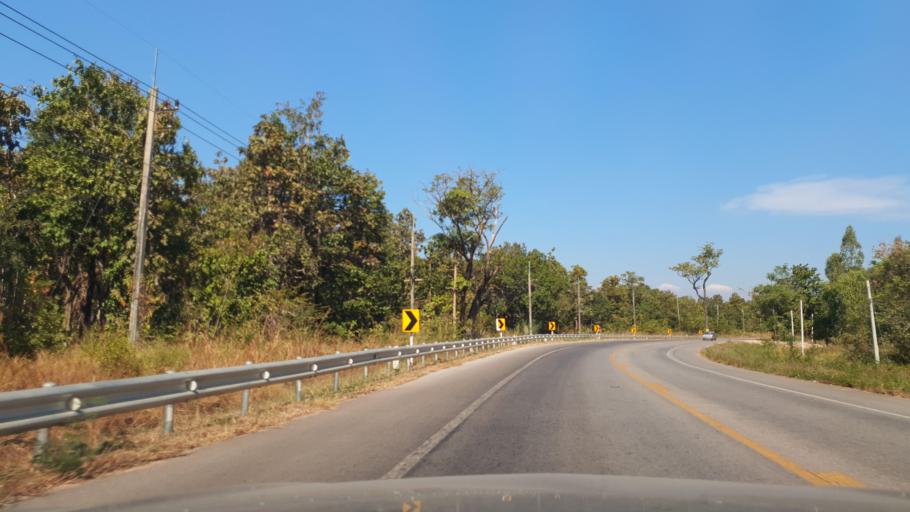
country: TH
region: Sakon Nakhon
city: Phu Phan
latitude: 17.0929
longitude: 103.9853
